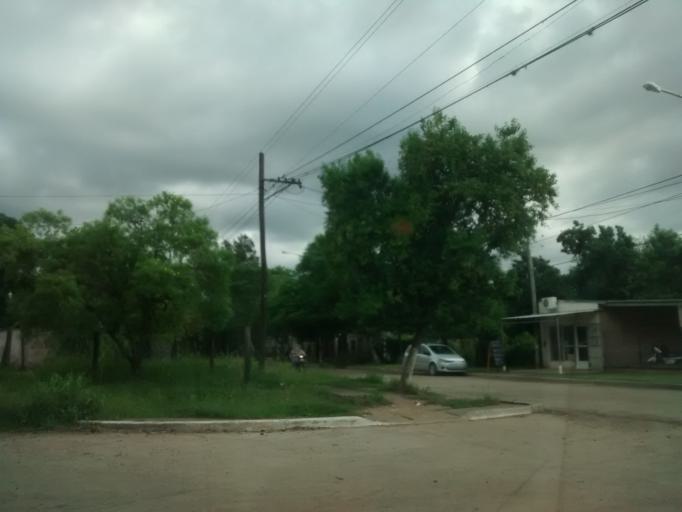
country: AR
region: Chaco
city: Puerto Tirol
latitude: -27.3779
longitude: -59.0863
